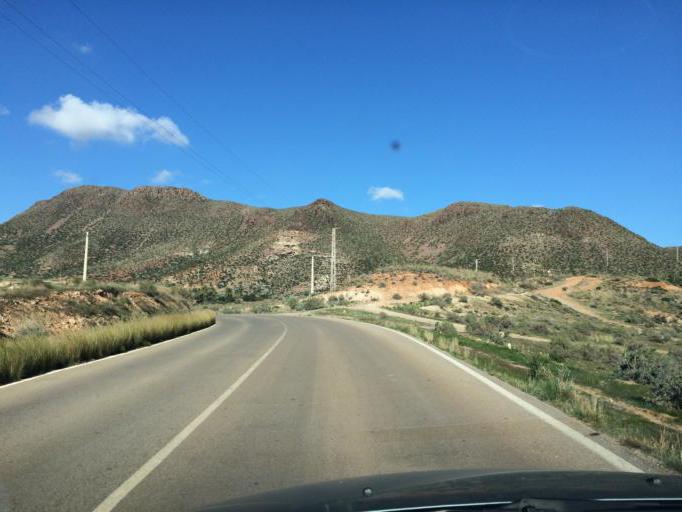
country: ES
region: Andalusia
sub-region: Provincia de Almeria
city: San Jose
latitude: 36.8171
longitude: -2.0530
